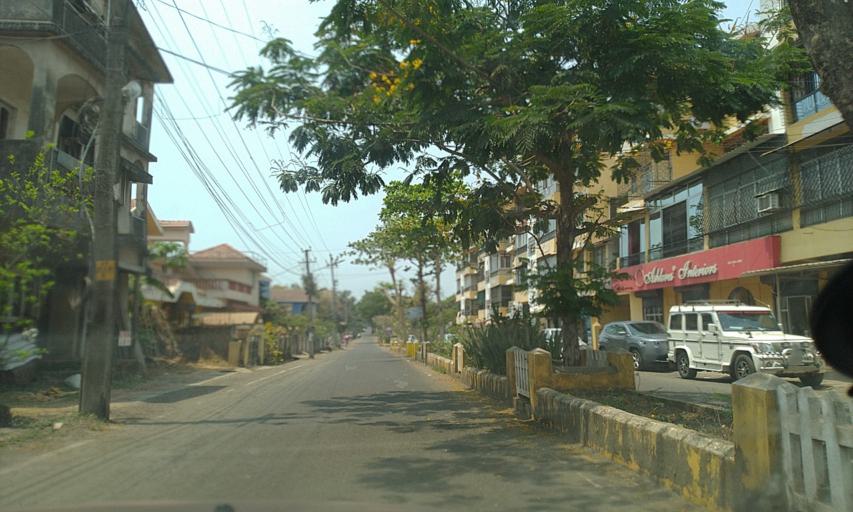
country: IN
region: Goa
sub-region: North Goa
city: Panaji
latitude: 15.5248
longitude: 73.8241
